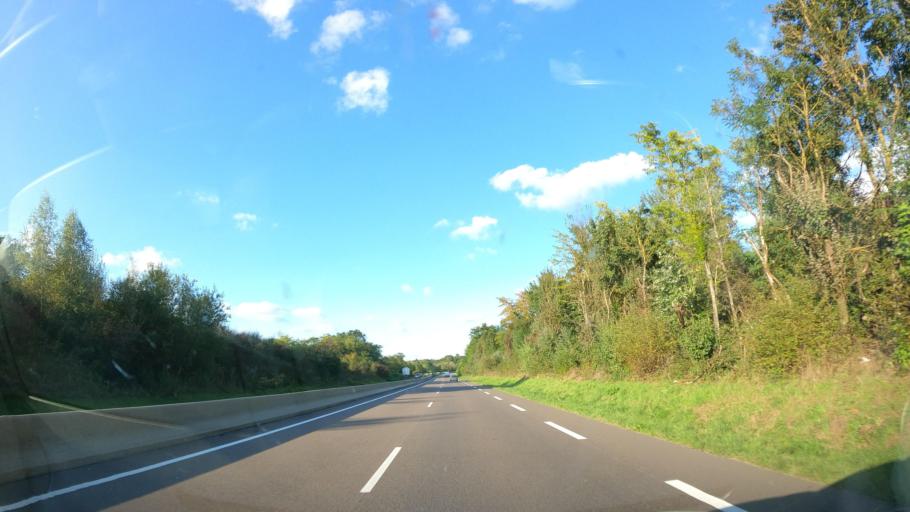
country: FR
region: Bourgogne
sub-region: Departement de Saone-et-Loire
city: Montceau-les-Mines
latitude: 46.6751
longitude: 4.3455
